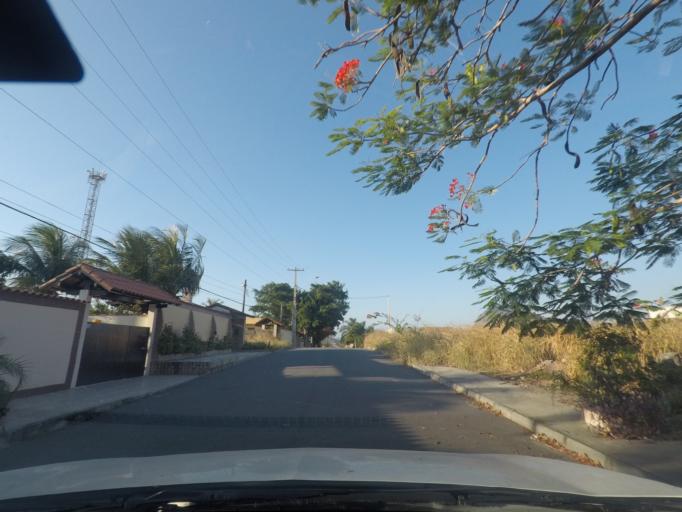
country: BR
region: Rio de Janeiro
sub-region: Marica
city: Marica
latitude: -22.9687
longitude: -42.9334
